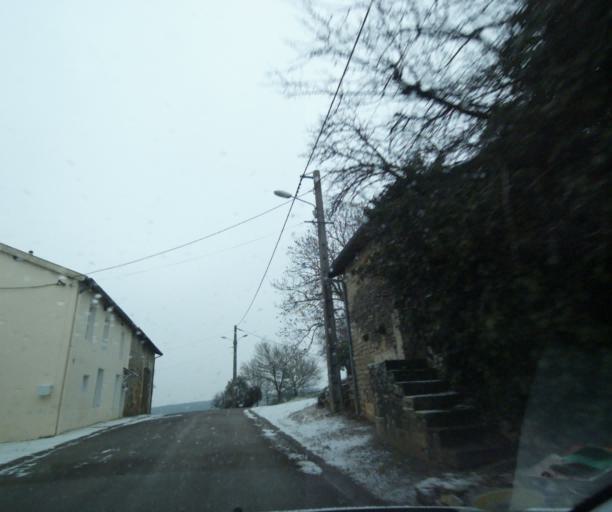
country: FR
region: Champagne-Ardenne
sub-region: Departement de la Haute-Marne
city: Wassy
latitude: 48.4604
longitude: 5.0307
